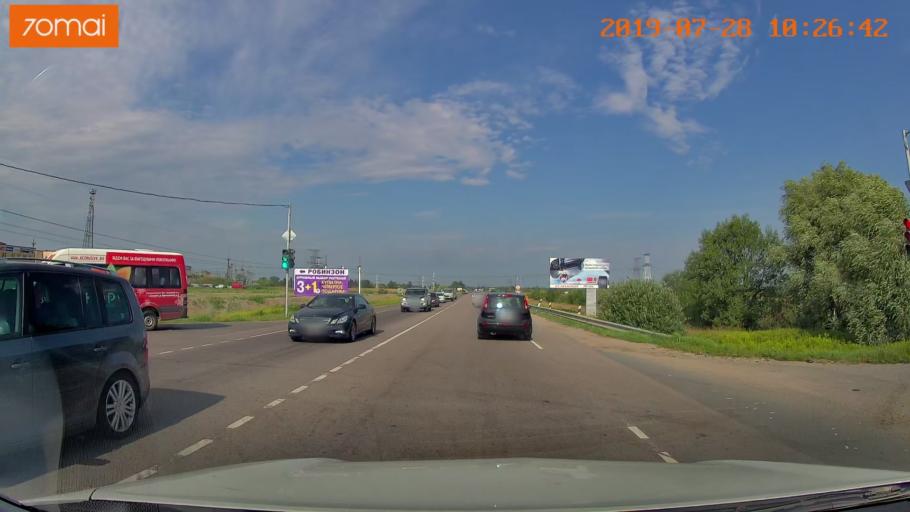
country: RU
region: Kaliningrad
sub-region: Gorod Kaliningrad
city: Kaliningrad
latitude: 54.7690
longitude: 20.5290
